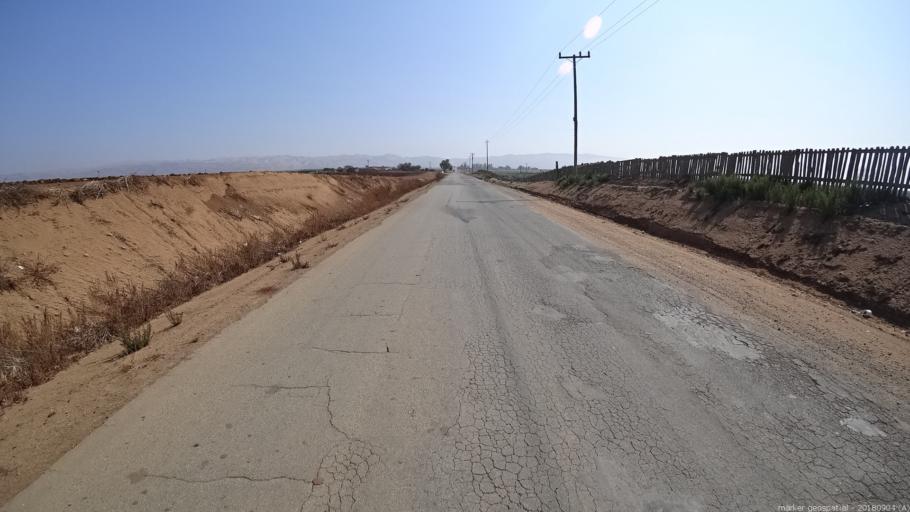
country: US
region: California
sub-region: Monterey County
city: Gonzales
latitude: 36.4968
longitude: -121.4163
